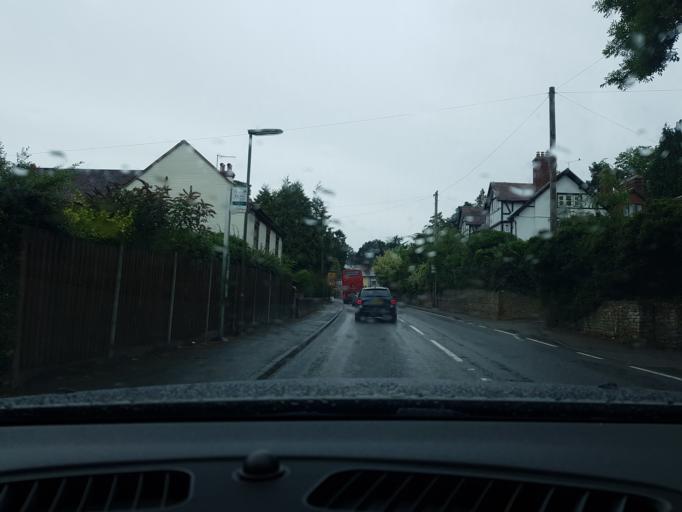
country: GB
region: England
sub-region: Surrey
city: Hale
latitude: 51.2334
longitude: -0.7932
